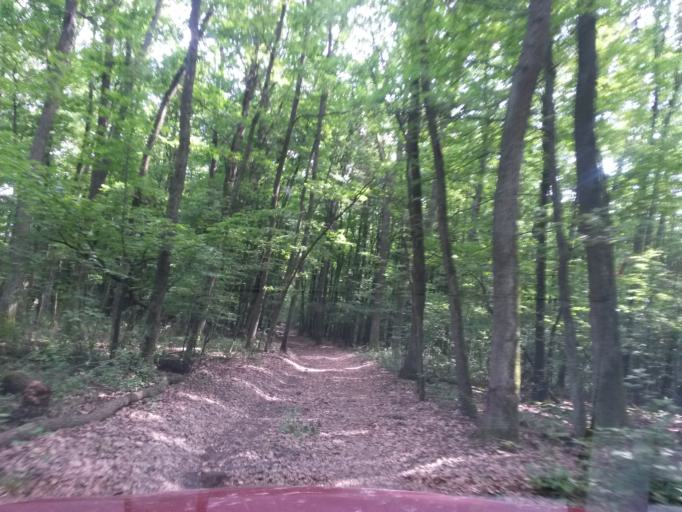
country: SK
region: Kosicky
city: Moldava nad Bodvou
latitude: 48.6270
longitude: 21.1000
